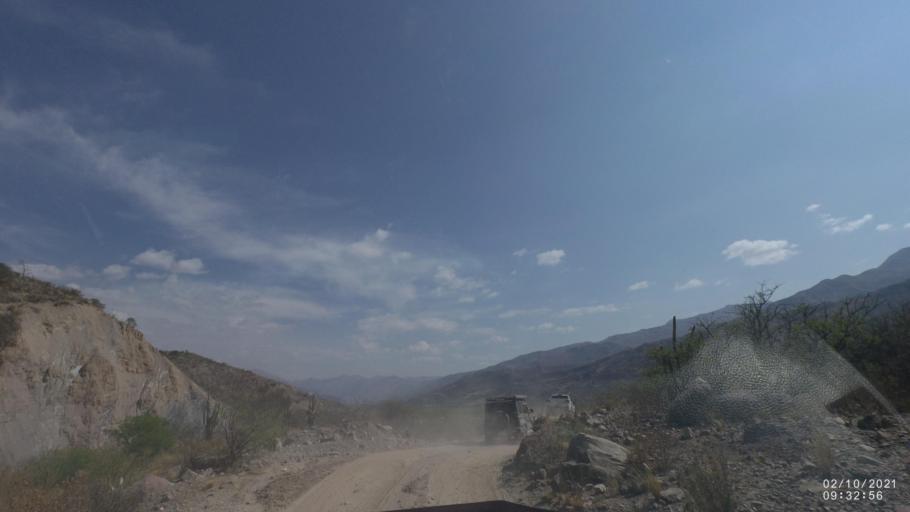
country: BO
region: Cochabamba
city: Irpa Irpa
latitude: -17.8444
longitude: -66.3201
